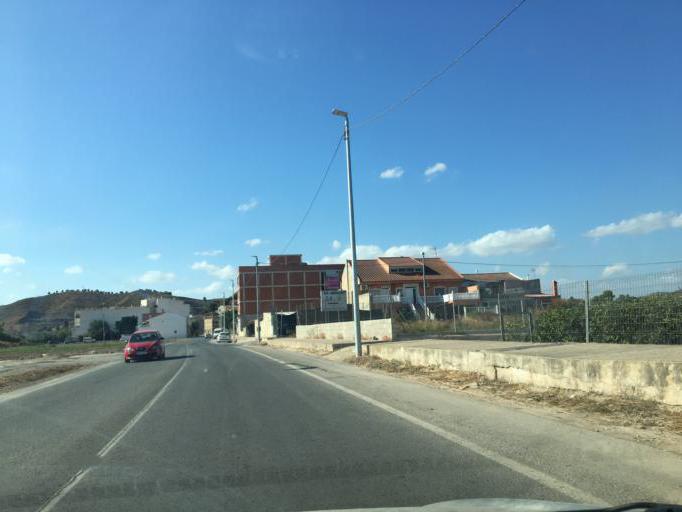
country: ES
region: Murcia
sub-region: Murcia
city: Murcia
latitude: 38.0208
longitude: -1.0865
